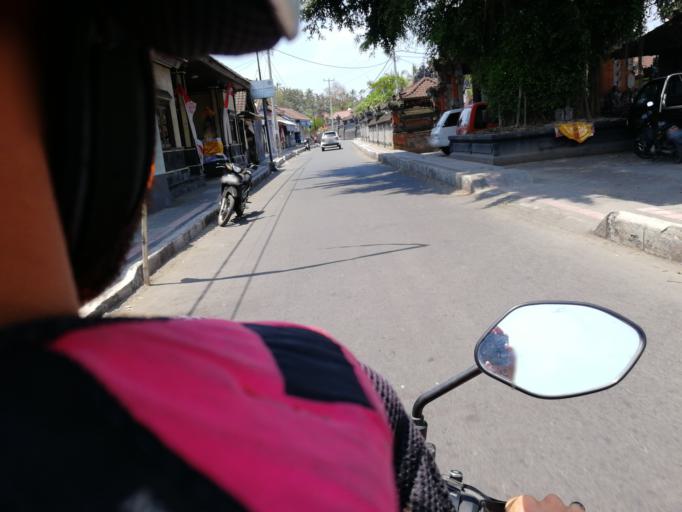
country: ID
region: Bali
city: Banjar Timbrah
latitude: -8.4773
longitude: 115.5966
